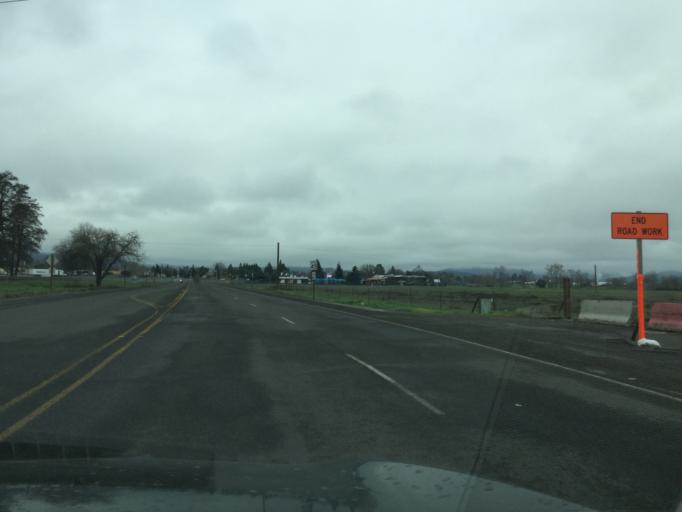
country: US
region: Oregon
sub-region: Jackson County
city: Central Point
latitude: 42.3794
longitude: -122.9003
